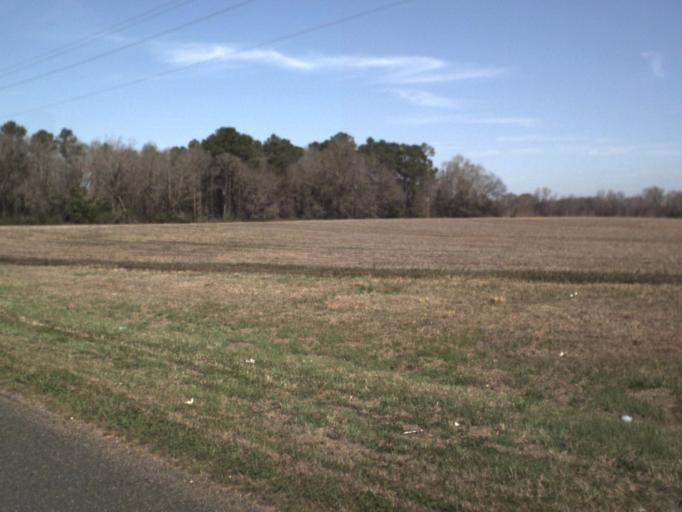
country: US
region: Florida
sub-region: Jackson County
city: Graceville
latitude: 30.9730
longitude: -85.4091
